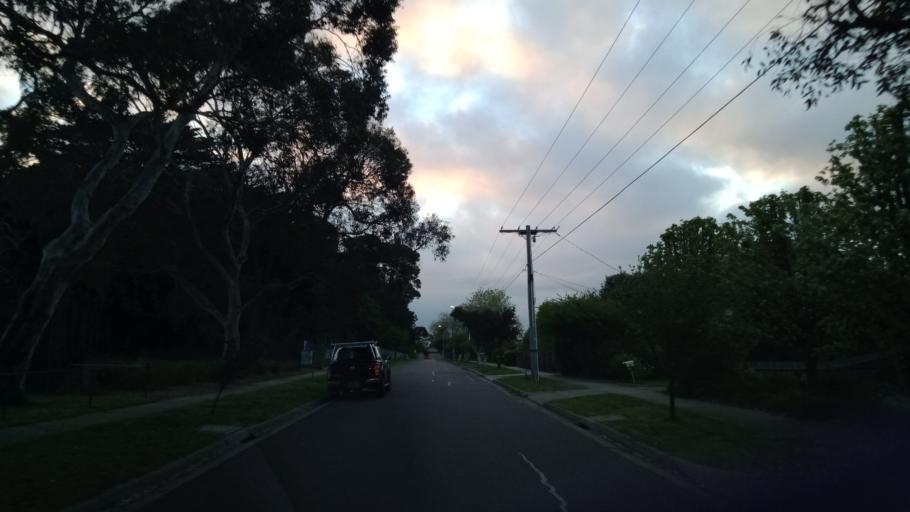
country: AU
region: Victoria
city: Burwood East
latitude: -37.8737
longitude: 145.1355
